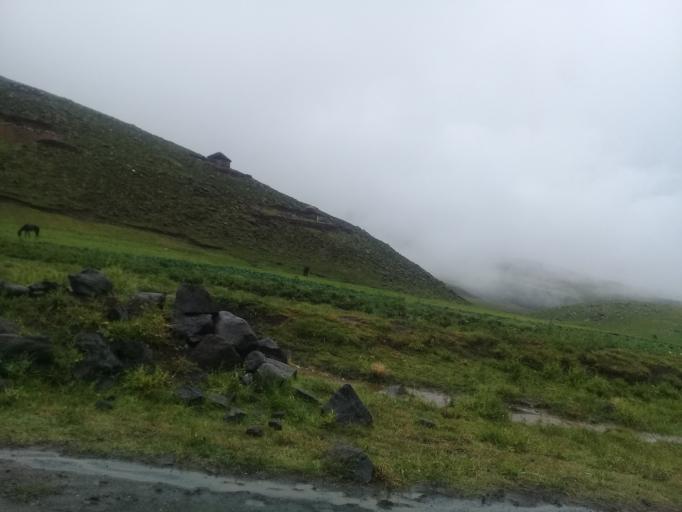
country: LS
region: Mokhotlong
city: Mokhotlong
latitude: -29.3857
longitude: 28.9792
